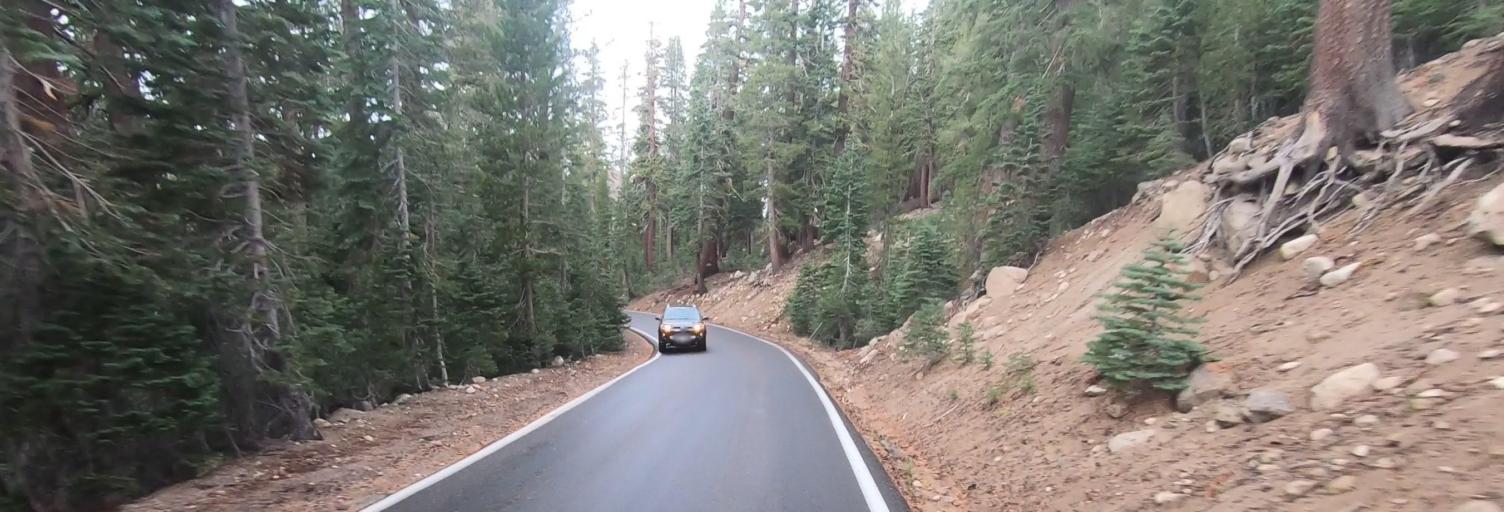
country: US
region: Nevada
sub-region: Douglas County
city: Gardnerville Ranchos
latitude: 38.5540
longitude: -119.8042
